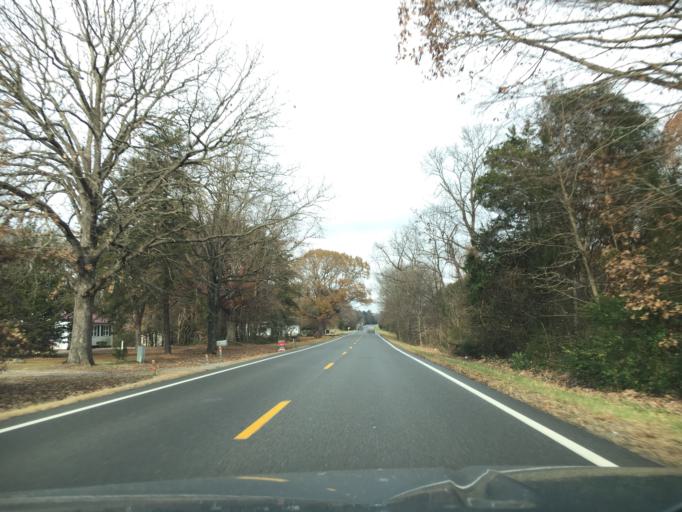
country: US
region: Virginia
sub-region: Prince Edward County
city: Farmville
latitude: 37.3525
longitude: -78.3809
